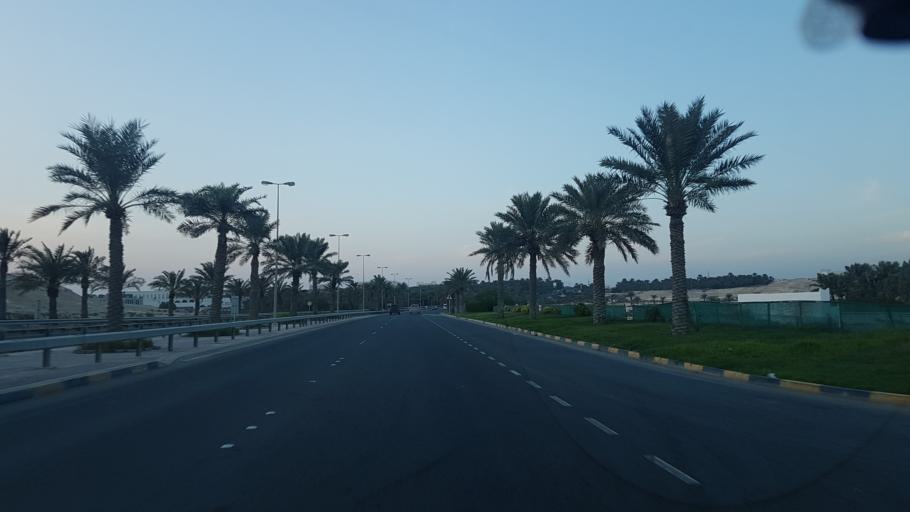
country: BH
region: Northern
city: Ar Rifa'
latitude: 26.1105
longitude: 50.5385
